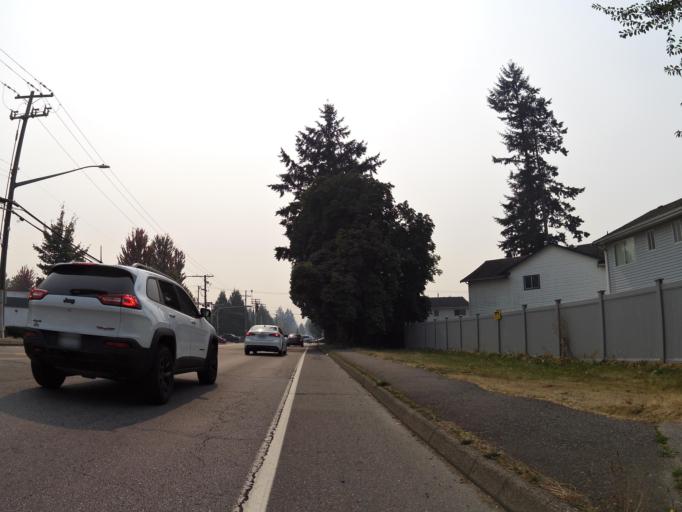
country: CA
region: British Columbia
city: Surrey
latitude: 49.1347
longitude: -122.8567
